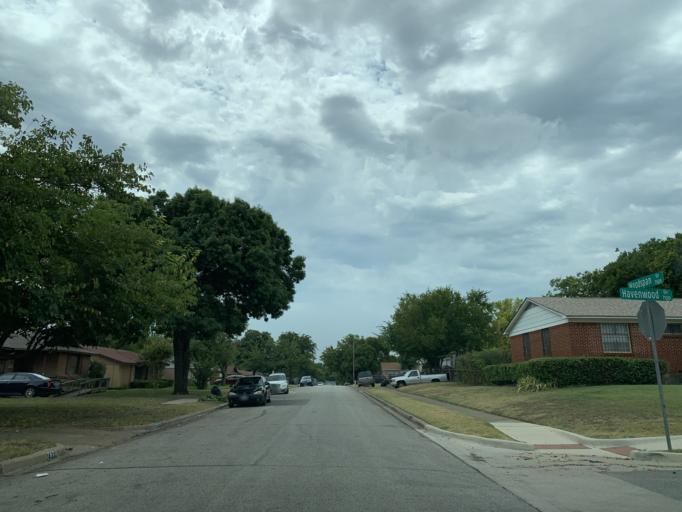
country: US
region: Texas
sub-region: Dallas County
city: DeSoto
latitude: 32.6566
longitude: -96.8319
